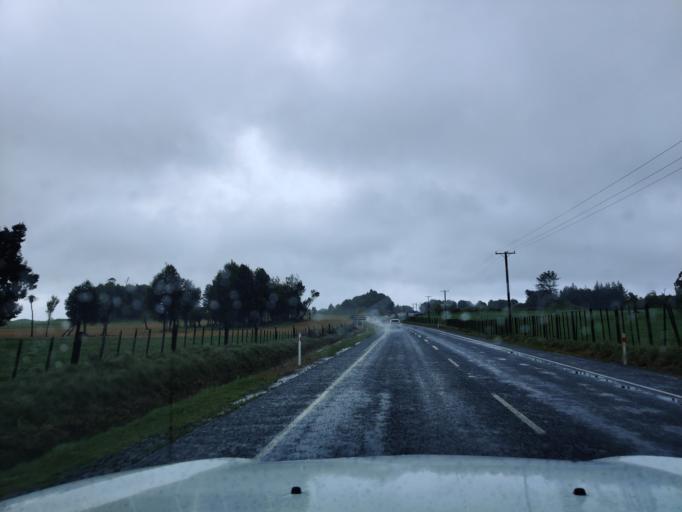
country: NZ
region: Bay of Plenty
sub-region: Rotorua District
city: Rotorua
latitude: -38.0526
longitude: 176.0808
